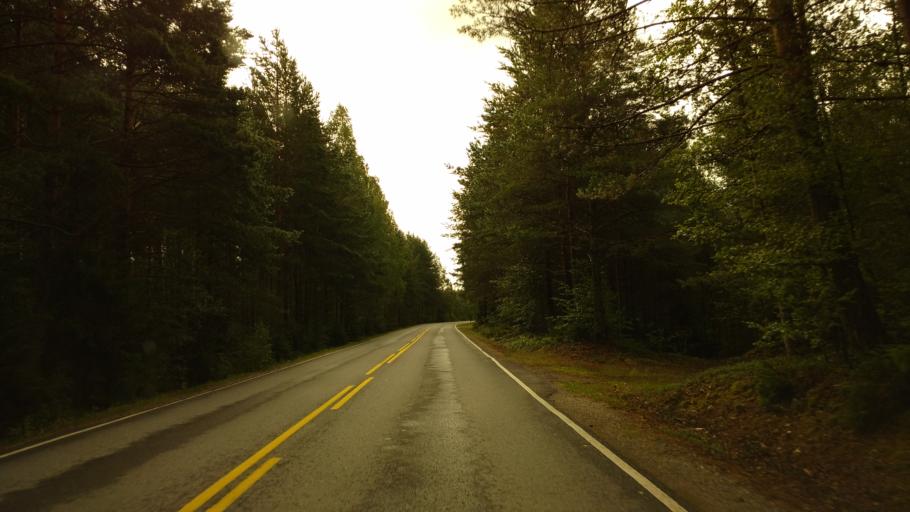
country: FI
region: Varsinais-Suomi
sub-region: Loimaa
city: Koski Tl
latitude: 60.6276
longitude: 23.1085
